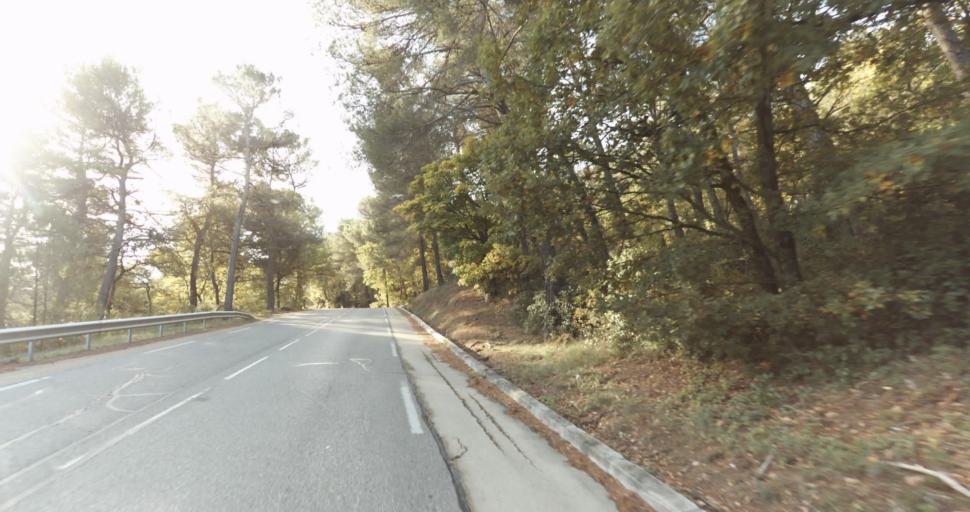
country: FR
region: Provence-Alpes-Cote d'Azur
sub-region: Departement des Bouches-du-Rhone
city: Venelles
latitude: 43.6167
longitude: 5.4632
